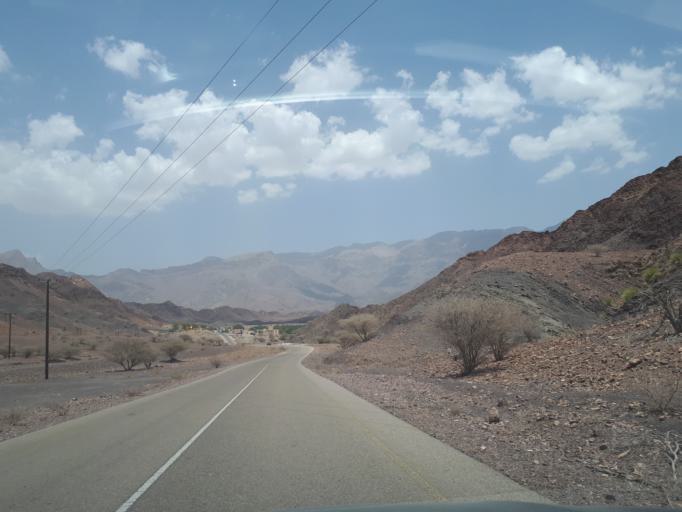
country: OM
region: Ash Sharqiyah
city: Badiyah
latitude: 22.4654
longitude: 59.1014
